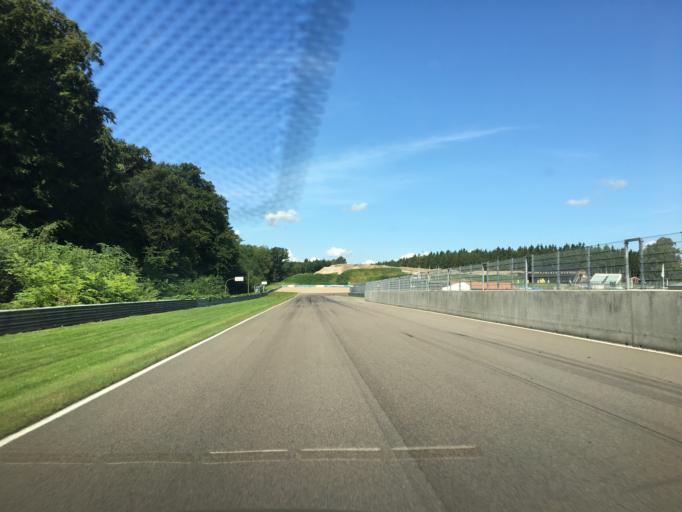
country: SE
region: Skane
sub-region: Svalovs Kommun
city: Kagerod
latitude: 55.9875
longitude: 13.1129
